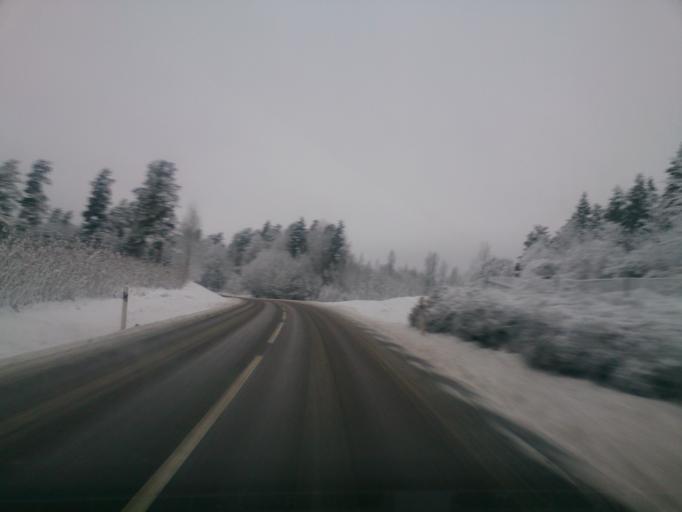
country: SE
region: OEstergoetland
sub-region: Atvidabergs Kommun
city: Atvidaberg
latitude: 58.3051
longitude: 15.8865
